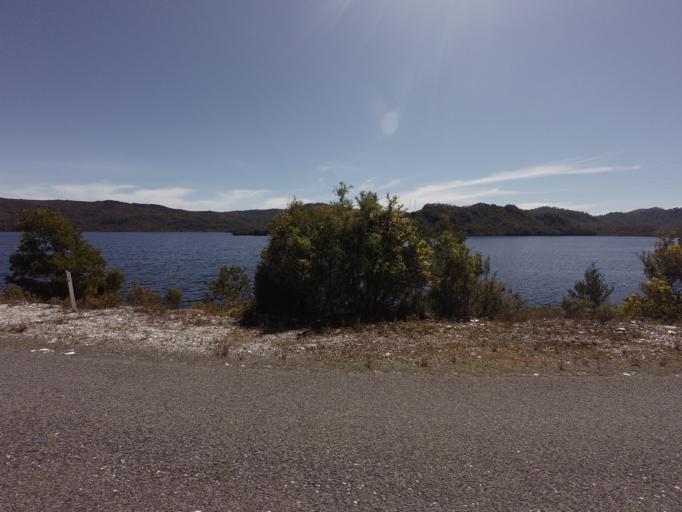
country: AU
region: Tasmania
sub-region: Huon Valley
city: Geeveston
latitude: -42.8305
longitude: 146.1261
